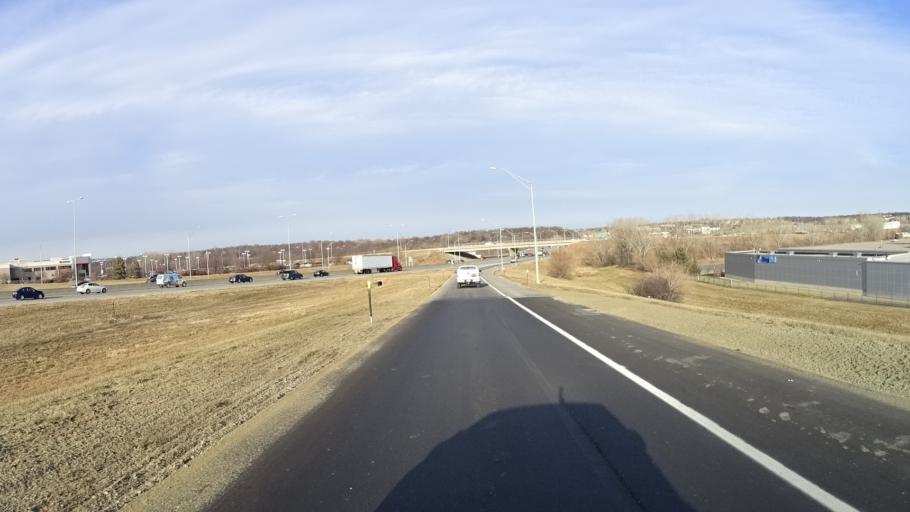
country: US
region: Nebraska
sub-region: Sarpy County
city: Chalco
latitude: 41.1860
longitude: -96.1066
